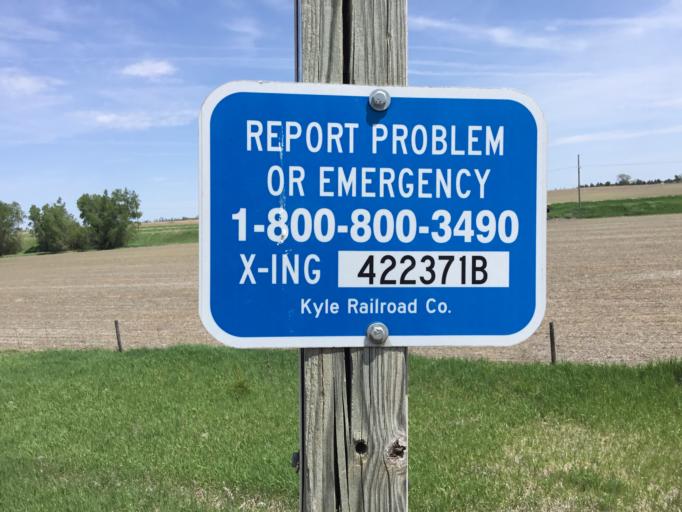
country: US
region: Kansas
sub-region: Mitchell County
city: Beloit
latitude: 39.4987
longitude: -98.2889
